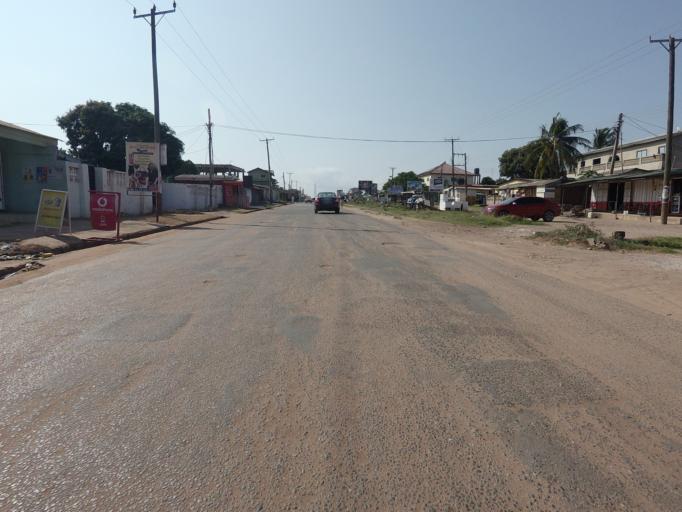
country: GH
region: Greater Accra
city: Teshi Old Town
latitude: 5.6044
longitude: -0.1050
